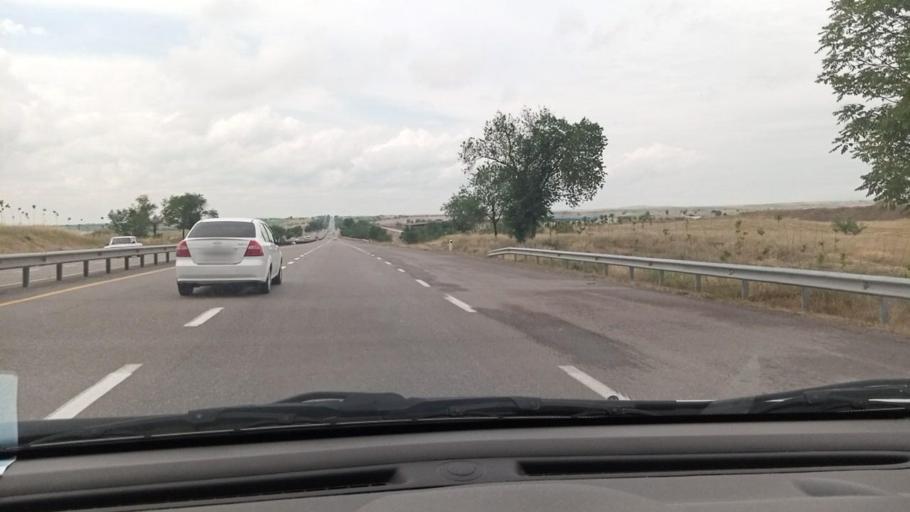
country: UZ
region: Toshkent
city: Ohangaron
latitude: 40.9861
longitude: 69.5367
